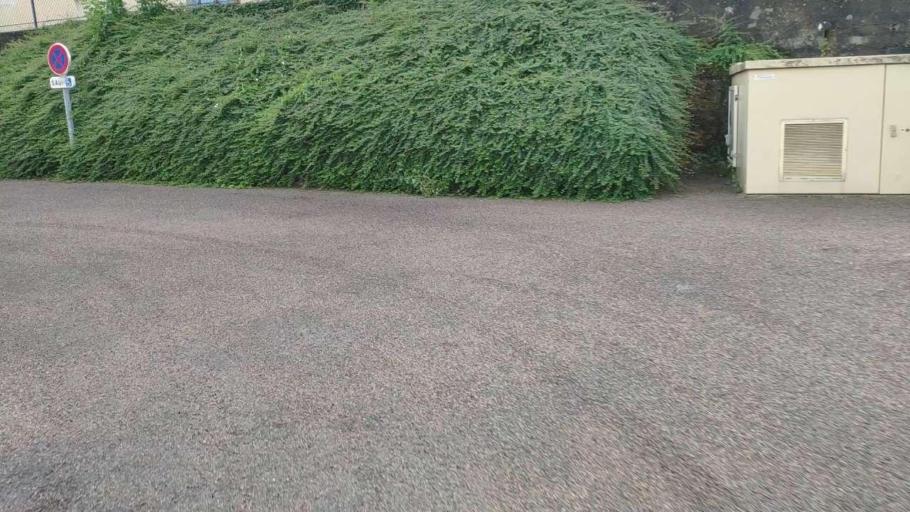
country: FR
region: Franche-Comte
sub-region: Departement du Jura
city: Poligny
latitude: 46.7984
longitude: 5.6182
